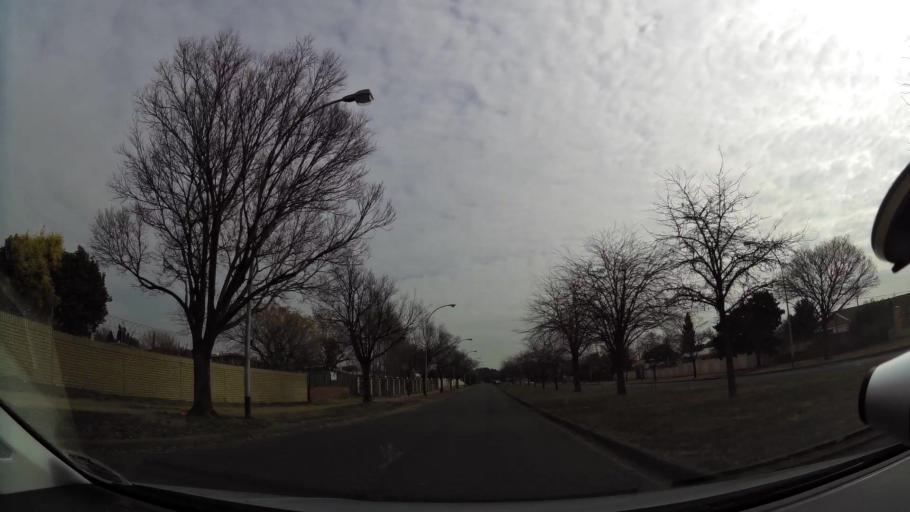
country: ZA
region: Orange Free State
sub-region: Mangaung Metropolitan Municipality
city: Bloemfontein
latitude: -29.1262
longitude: 26.2004
